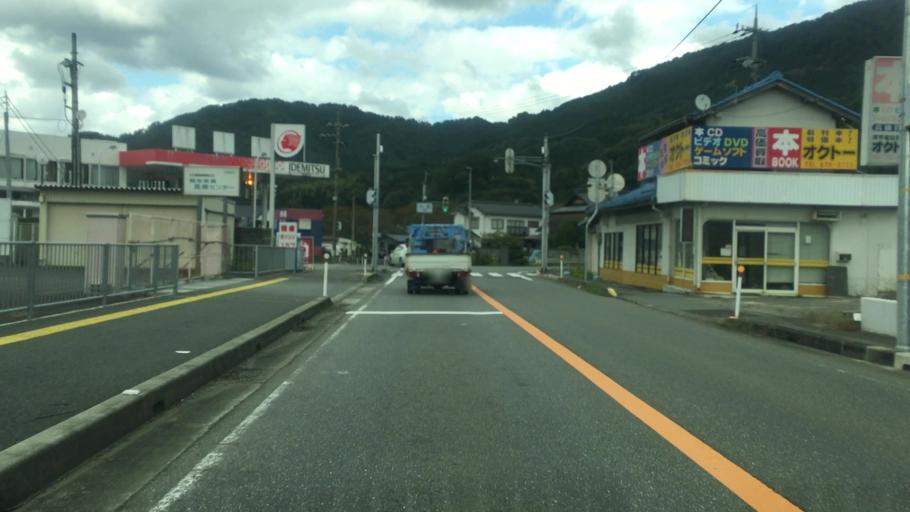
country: JP
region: Hyogo
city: Toyooka
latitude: 35.3184
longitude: 134.8826
